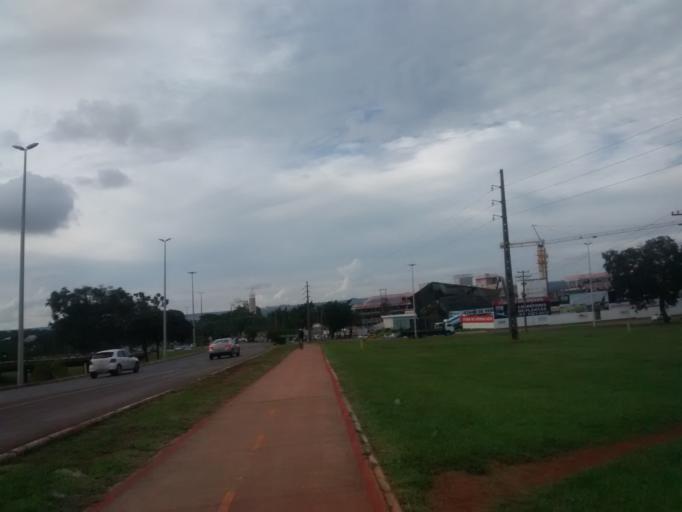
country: BR
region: Federal District
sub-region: Brasilia
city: Brasilia
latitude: -15.7908
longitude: -47.8735
